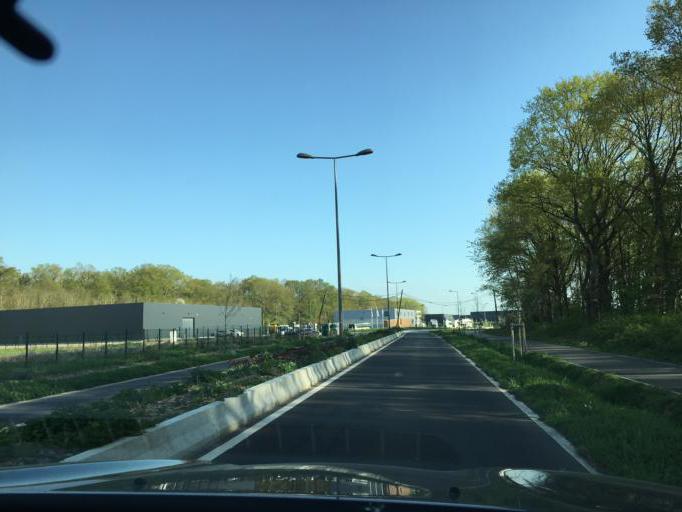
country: FR
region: Centre
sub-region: Departement du Loiret
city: Gidy
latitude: 47.9682
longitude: 1.8478
